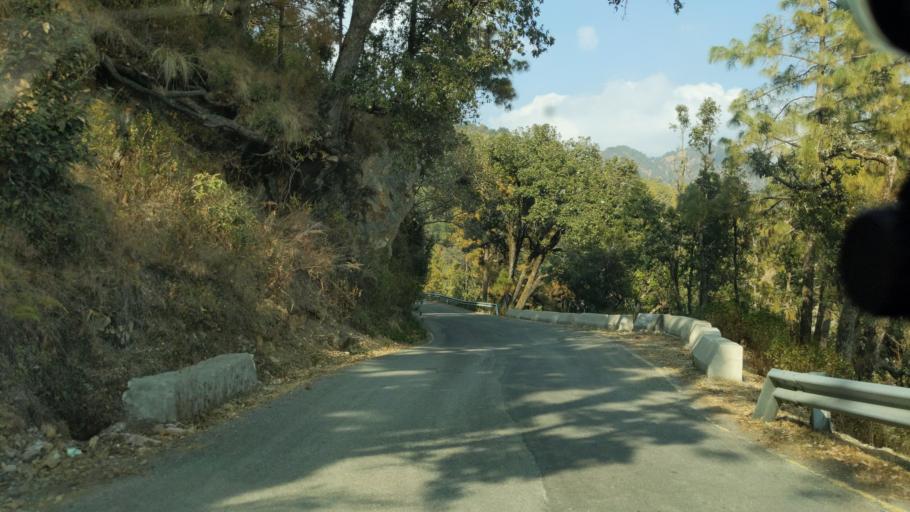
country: IN
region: Uttarakhand
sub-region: Naini Tal
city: Bhowali
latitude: 29.3996
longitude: 79.5352
